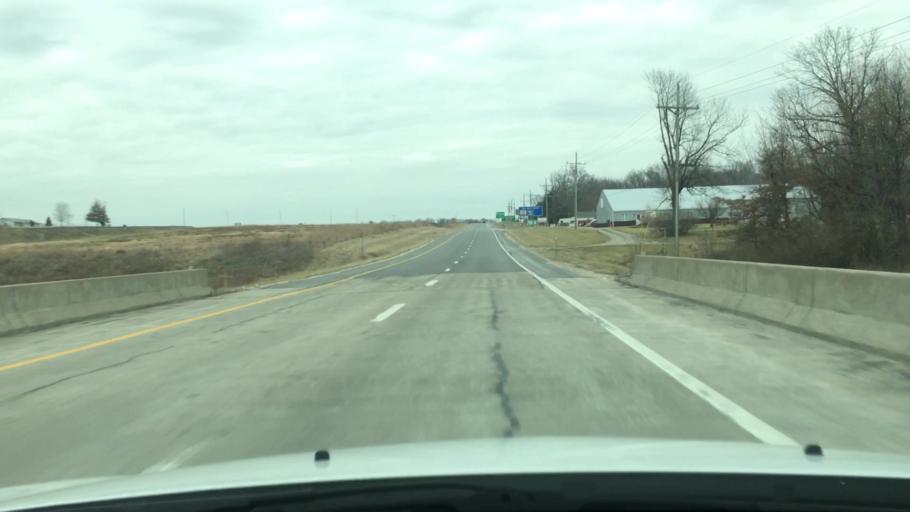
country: US
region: Missouri
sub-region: Audrain County
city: Mexico
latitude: 39.1073
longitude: -91.8956
